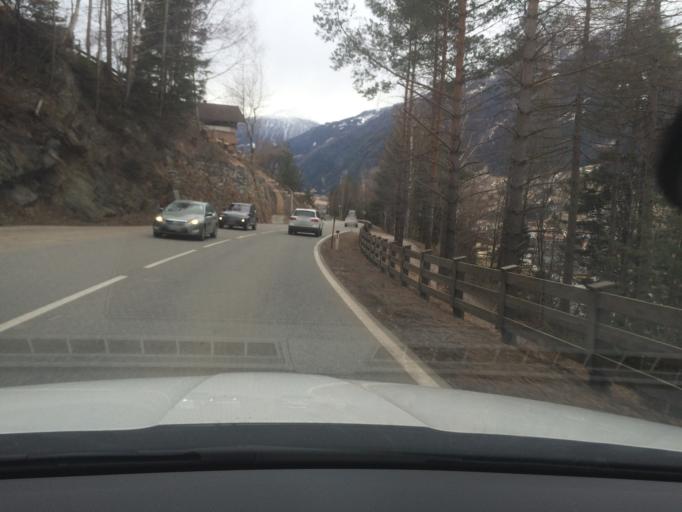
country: AT
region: Tyrol
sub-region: Politischer Bezirk Lienz
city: Matrei in Osttirol
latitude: 47.0075
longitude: 12.5404
